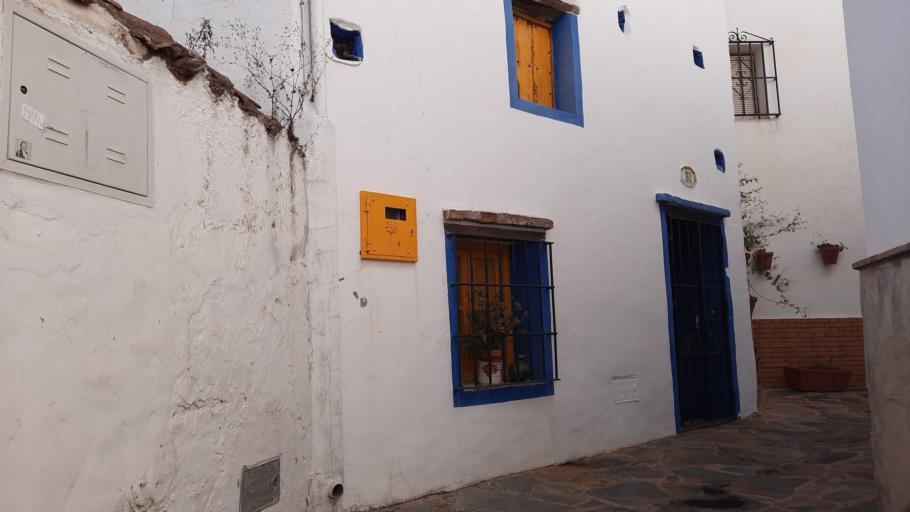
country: ES
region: Andalusia
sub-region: Provincia de Malaga
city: Gaucin
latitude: 36.5191
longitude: -5.3180
